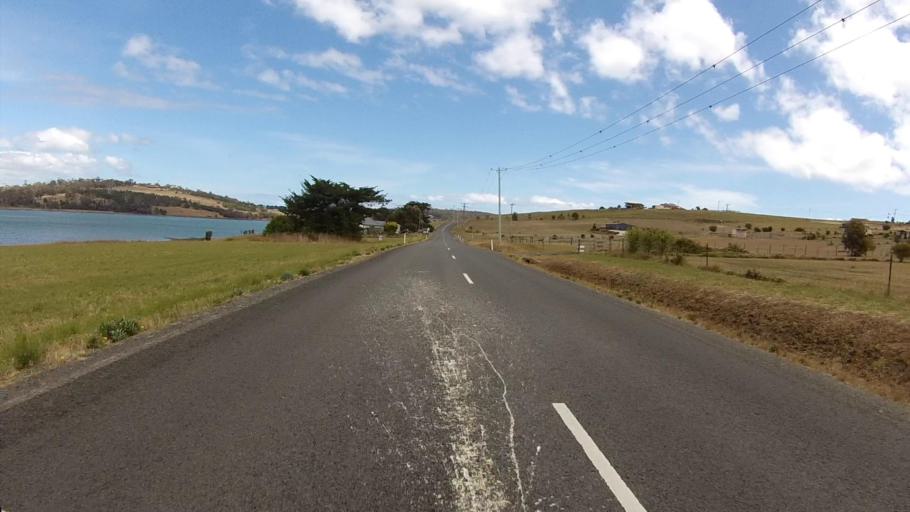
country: AU
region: Tasmania
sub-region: Sorell
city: Sorell
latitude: -42.8667
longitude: 147.6758
